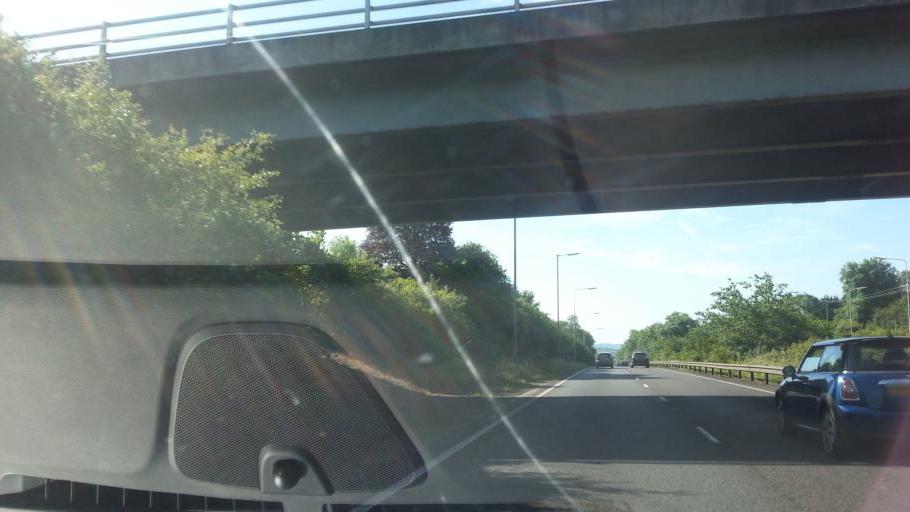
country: GB
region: England
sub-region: Central Bedfordshire
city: Edworth
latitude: 52.0486
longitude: -0.2268
